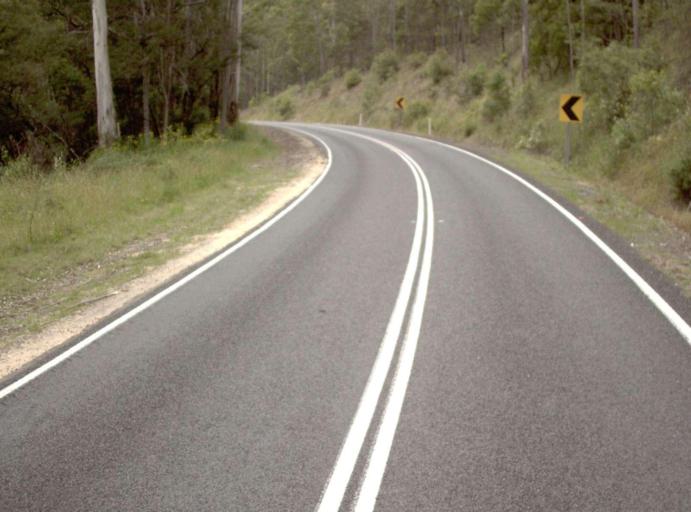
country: AU
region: New South Wales
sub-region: Bombala
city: Bombala
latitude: -37.4184
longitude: 149.1987
